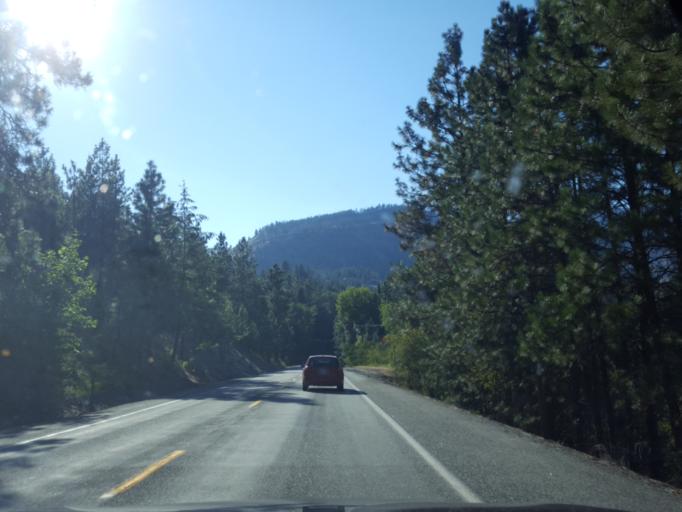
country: US
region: Washington
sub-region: Chelan County
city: Granite Falls
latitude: 47.8698
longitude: -120.1924
